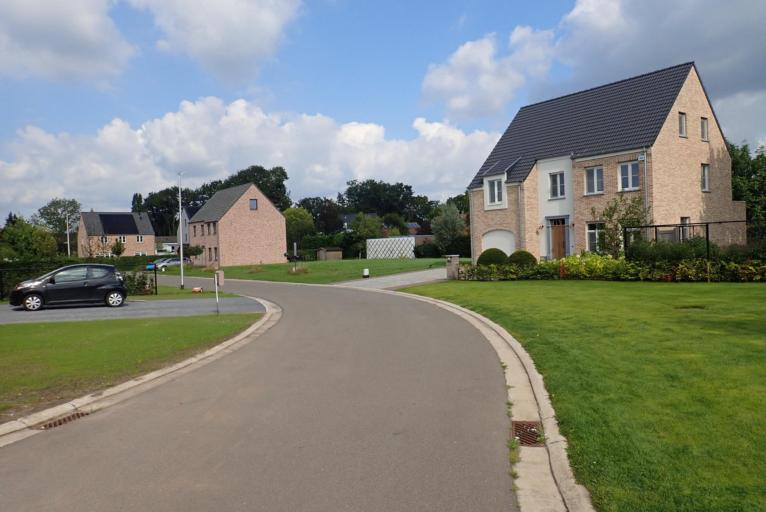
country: BE
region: Flanders
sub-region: Provincie Antwerpen
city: Essen
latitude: 51.4255
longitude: 4.4564
